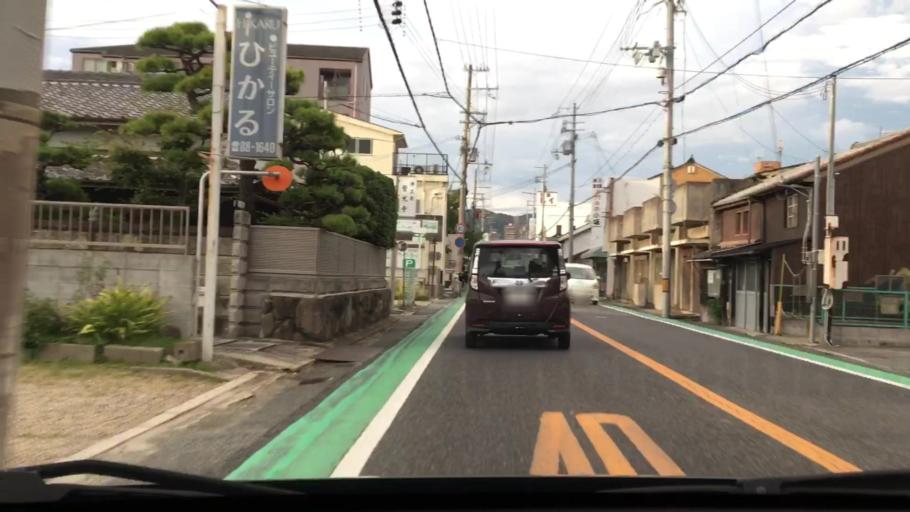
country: JP
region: Hyogo
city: Himeji
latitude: 34.8436
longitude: 134.6995
